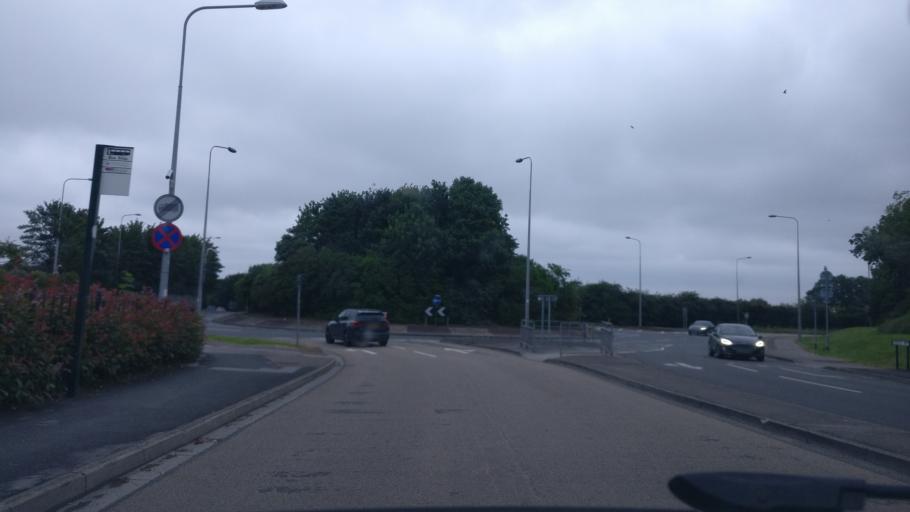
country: GB
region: England
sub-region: East Riding of Yorkshire
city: Beverley
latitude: 53.8247
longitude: -0.4417
